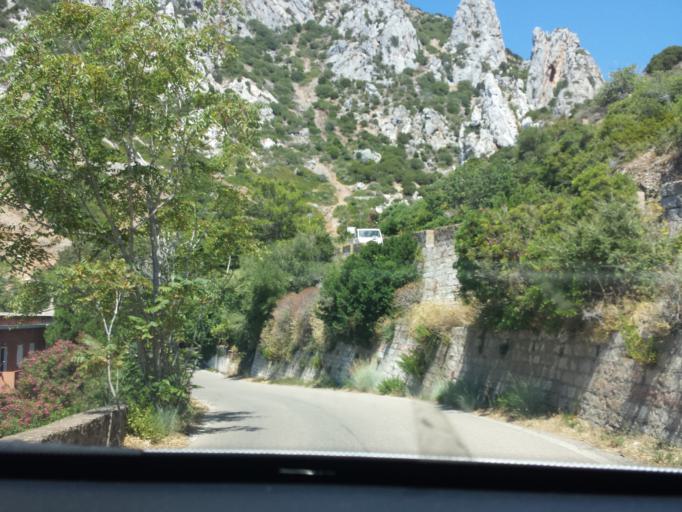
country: IT
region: Sardinia
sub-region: Provincia di Carbonia-Iglesias
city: Buggerru
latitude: 39.3310
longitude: 8.4341
